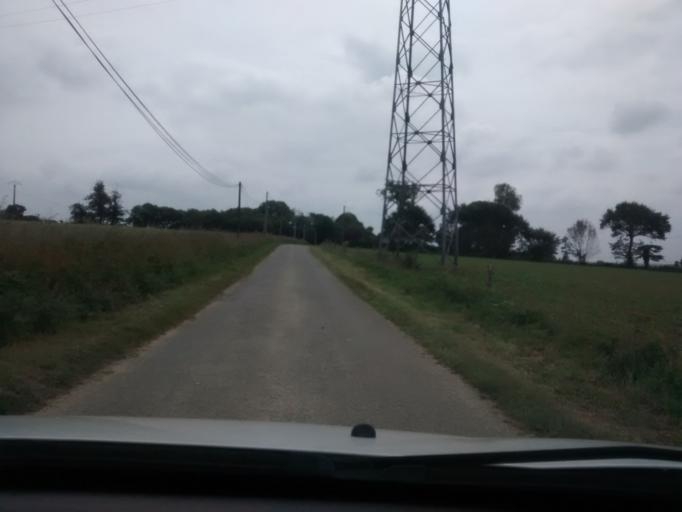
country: FR
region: Brittany
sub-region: Departement d'Ille-et-Vilaine
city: Servon-sur-Vilaine
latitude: 48.1326
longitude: -1.4661
